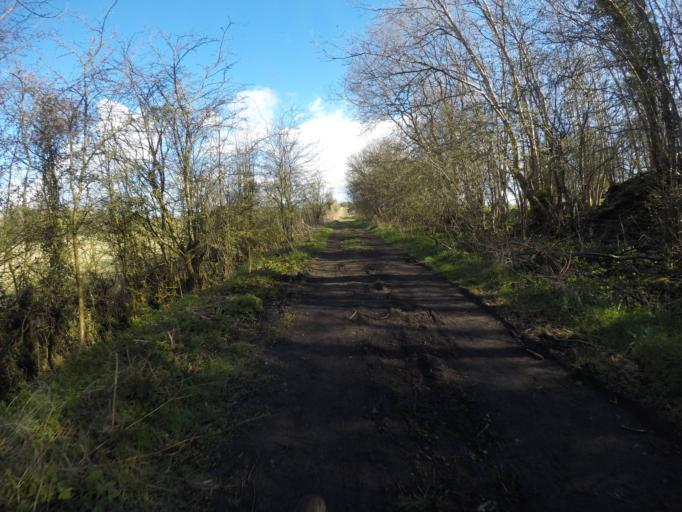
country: GB
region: Scotland
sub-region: North Ayrshire
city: Irvine
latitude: 55.6491
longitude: -4.6591
